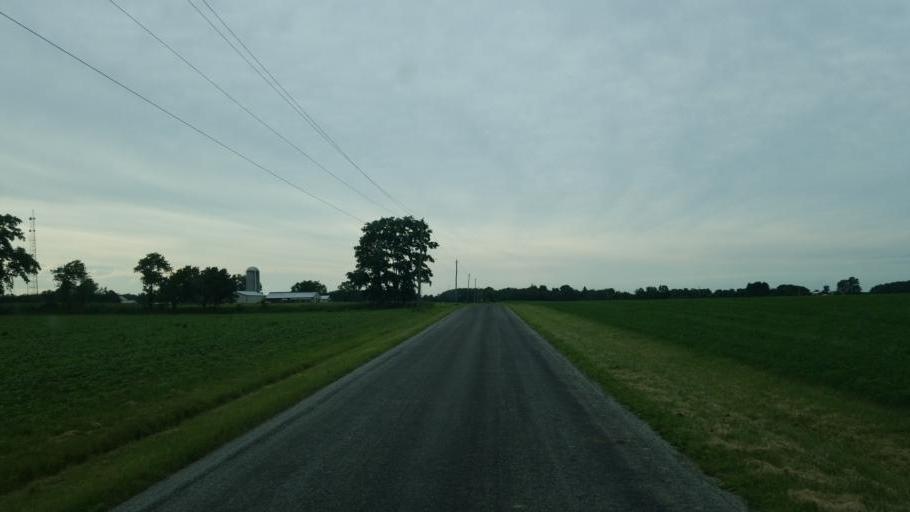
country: US
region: Ohio
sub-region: Huron County
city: Greenwich
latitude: 40.9340
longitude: -82.4750
